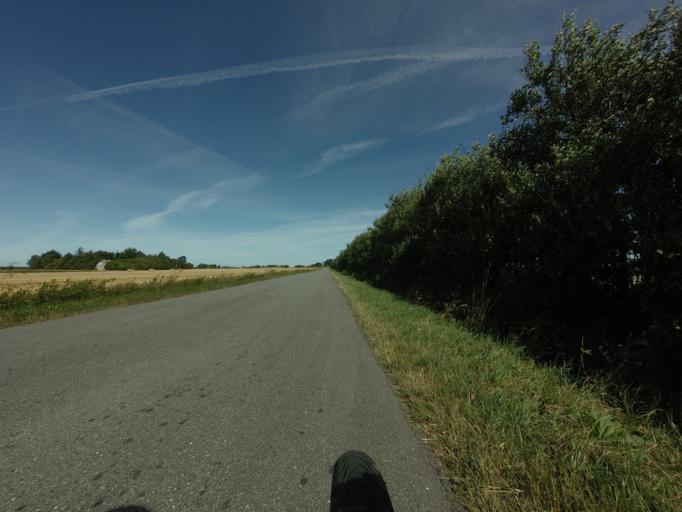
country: DK
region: North Denmark
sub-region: Bronderslev Kommune
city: Bronderslev
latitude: 57.3207
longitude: 9.8155
